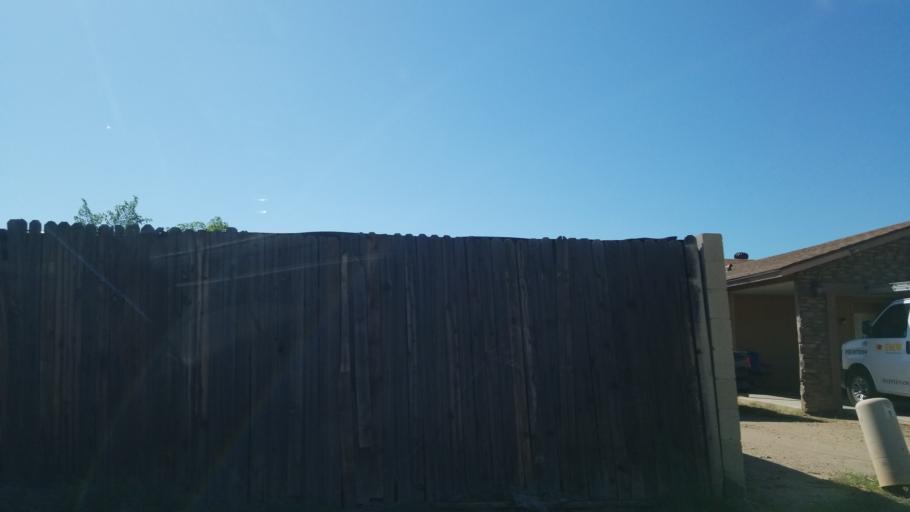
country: US
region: Arizona
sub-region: Maricopa County
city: Glendale
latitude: 33.4768
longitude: -112.1581
